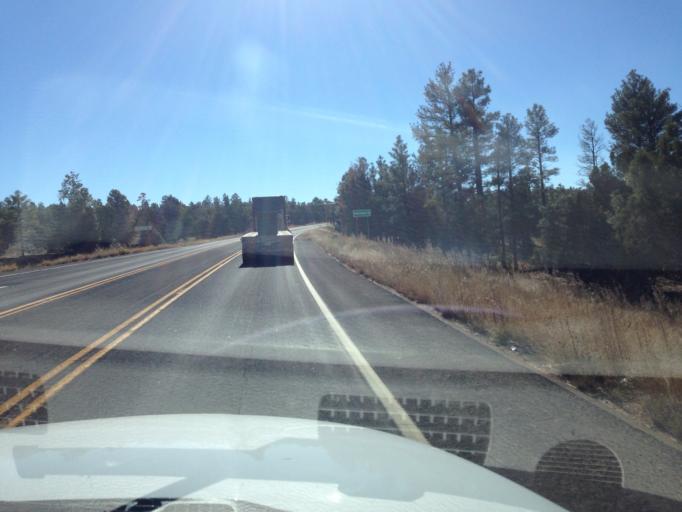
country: US
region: Arizona
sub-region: Navajo County
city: Linden
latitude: 34.2764
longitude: -110.0952
